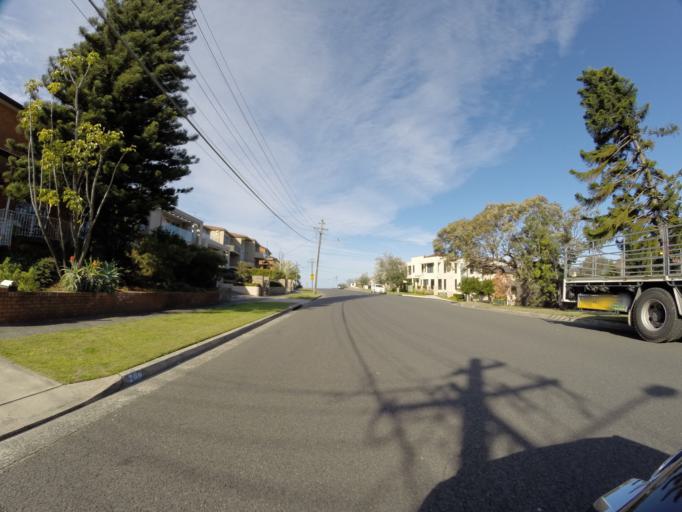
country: AU
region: New South Wales
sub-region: Randwick
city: South Coogee
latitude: -33.9397
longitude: 151.2505
